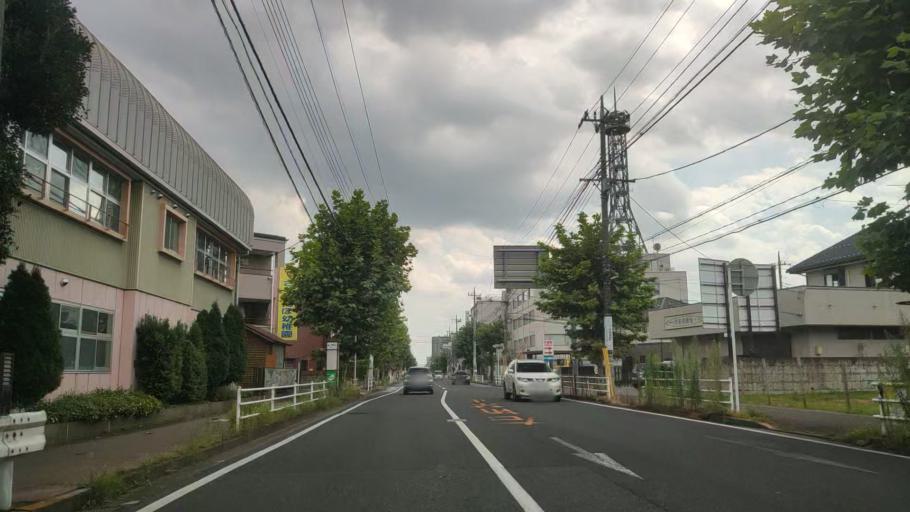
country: JP
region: Tochigi
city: Utsunomiya-shi
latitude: 36.5734
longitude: 139.8706
